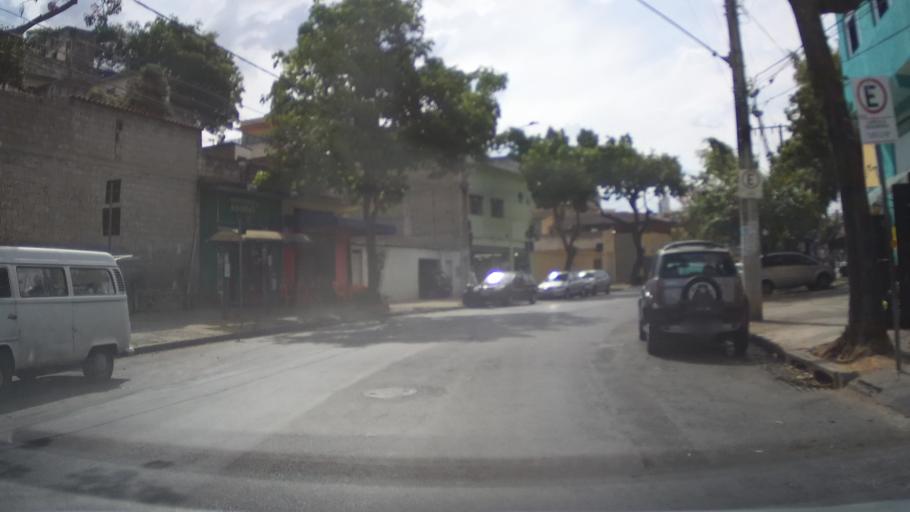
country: BR
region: Minas Gerais
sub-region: Belo Horizonte
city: Belo Horizonte
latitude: -19.9035
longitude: -43.9194
